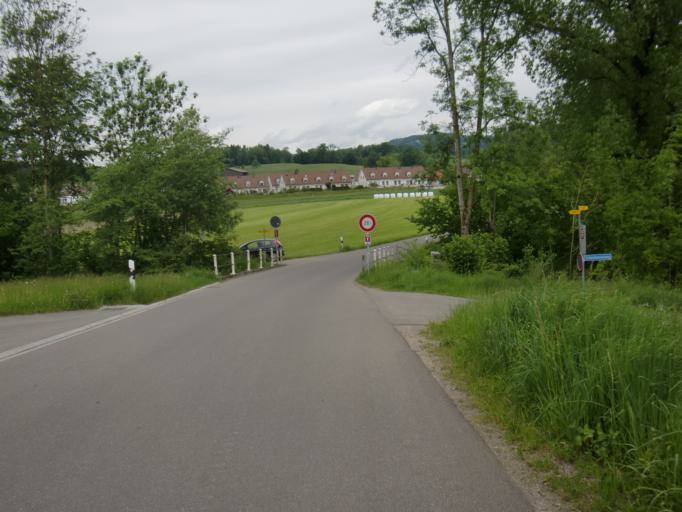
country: CH
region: Zurich
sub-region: Bezirk Hinwil
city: Durnten
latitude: 47.2726
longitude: 8.8363
